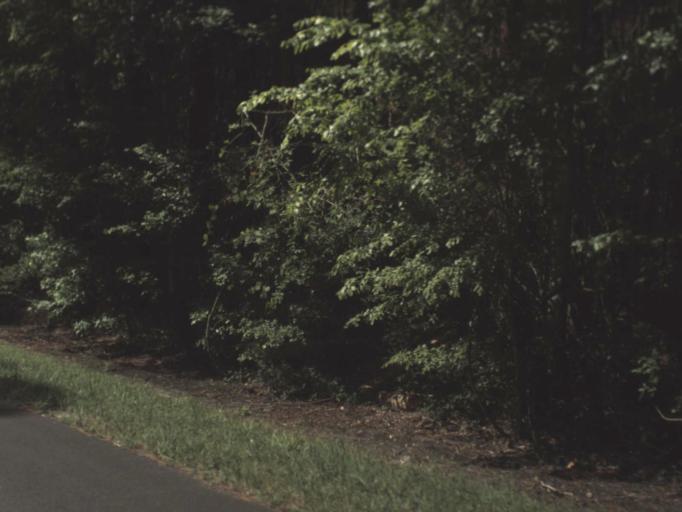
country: US
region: Florida
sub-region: Nassau County
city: Nassau Village-Ratliff
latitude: 30.4692
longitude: -81.7084
